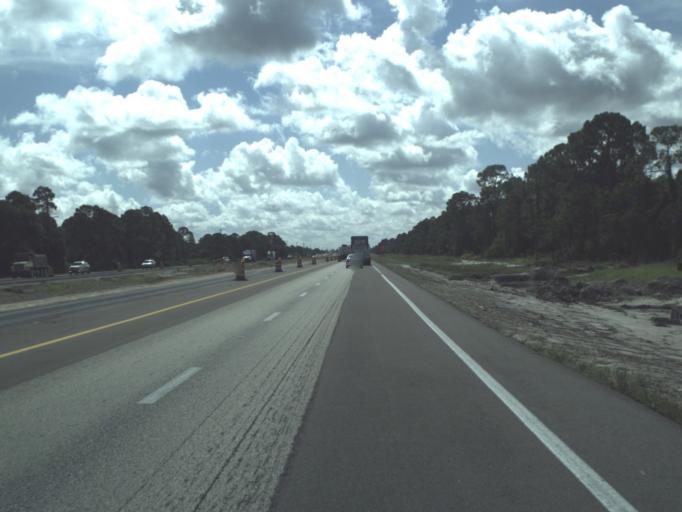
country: US
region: Florida
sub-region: Charlotte County
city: Port Charlotte
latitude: 27.0684
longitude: -82.0947
